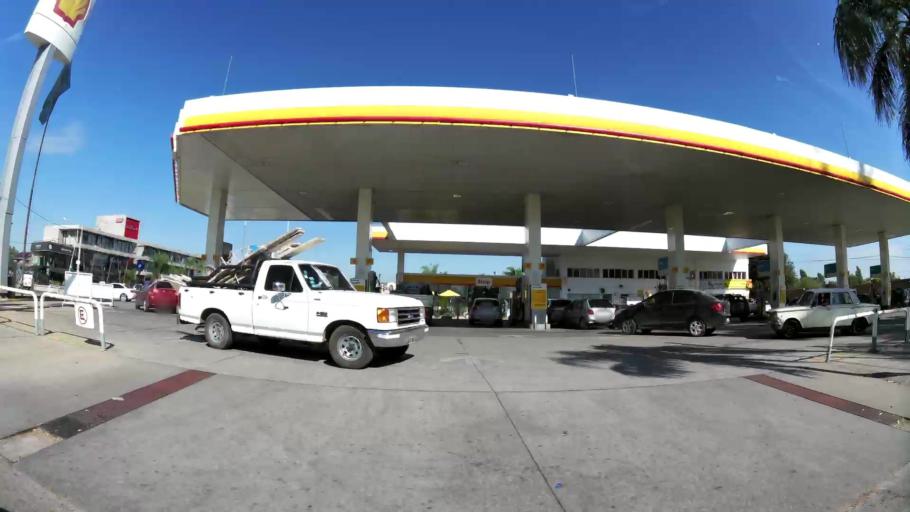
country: AR
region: Cordoba
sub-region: Departamento de Capital
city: Cordoba
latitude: -31.4650
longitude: -64.1869
